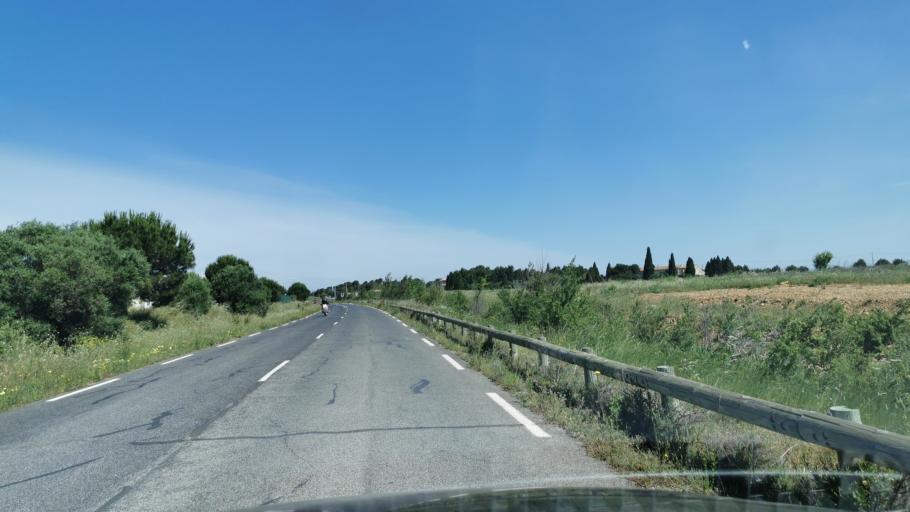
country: FR
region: Languedoc-Roussillon
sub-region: Departement de l'Aude
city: Narbonne
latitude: 43.1551
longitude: 2.9967
